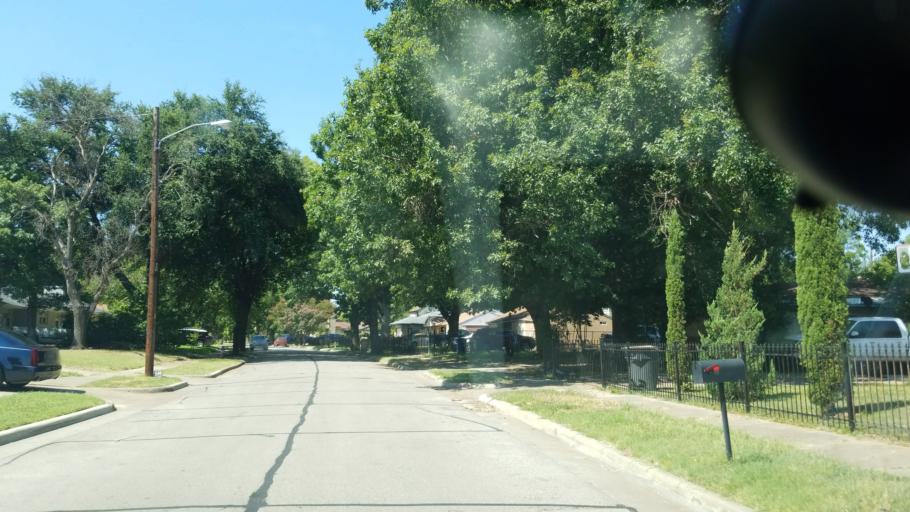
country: US
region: Texas
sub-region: Dallas County
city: Cockrell Hill
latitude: 32.7166
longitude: -96.8381
